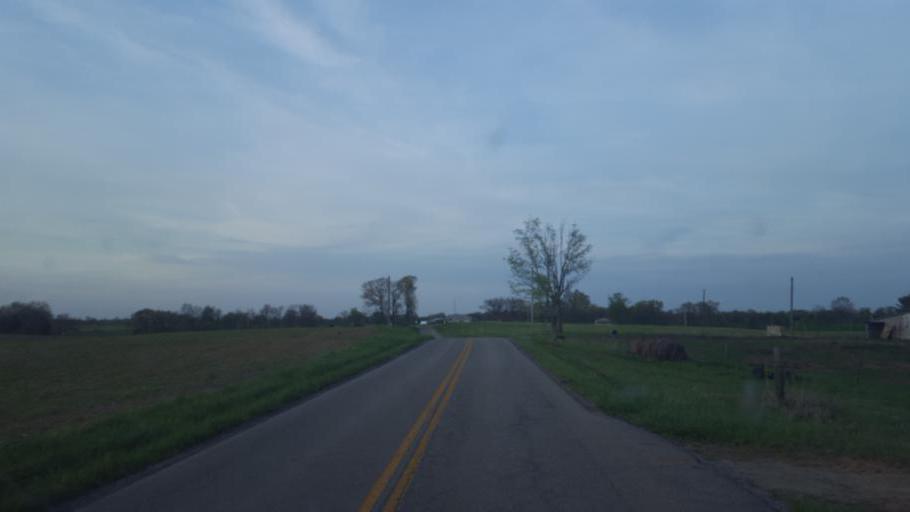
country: US
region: Kentucky
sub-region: Metcalfe County
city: Edmonton
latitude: 37.1047
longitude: -85.6984
